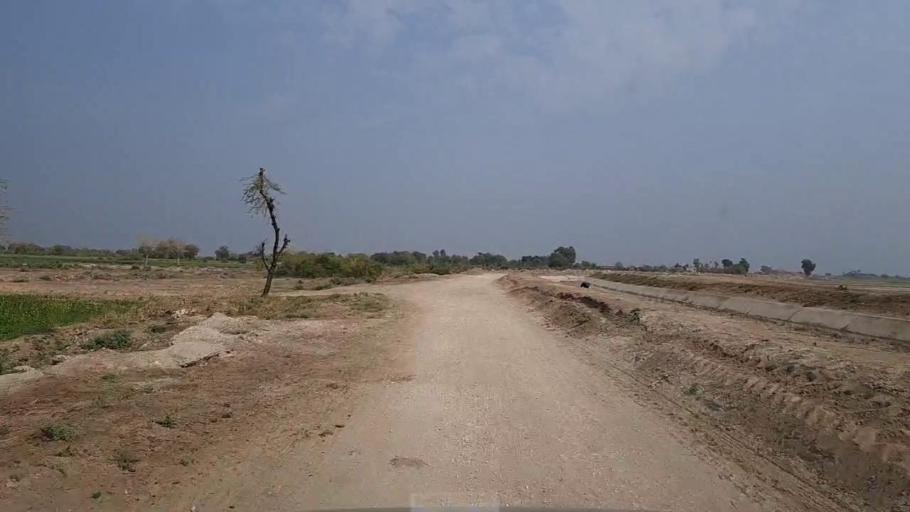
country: PK
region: Sindh
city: Mirwah Gorchani
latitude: 25.3998
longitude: 69.0799
